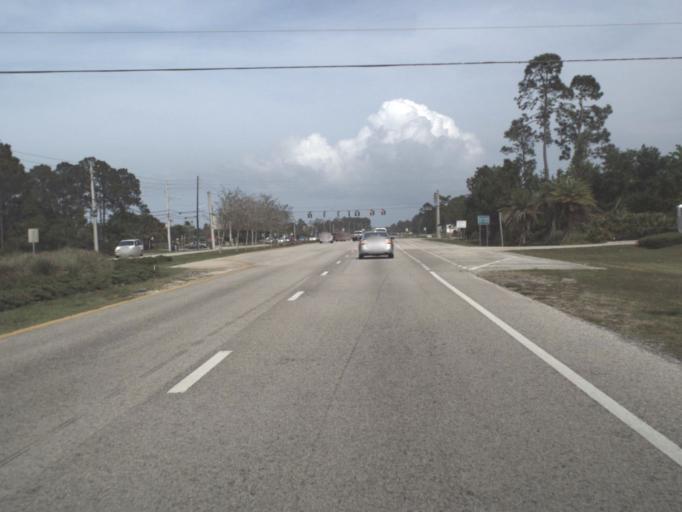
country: US
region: Florida
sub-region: Flagler County
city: Bunnell
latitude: 29.4756
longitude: -81.2241
